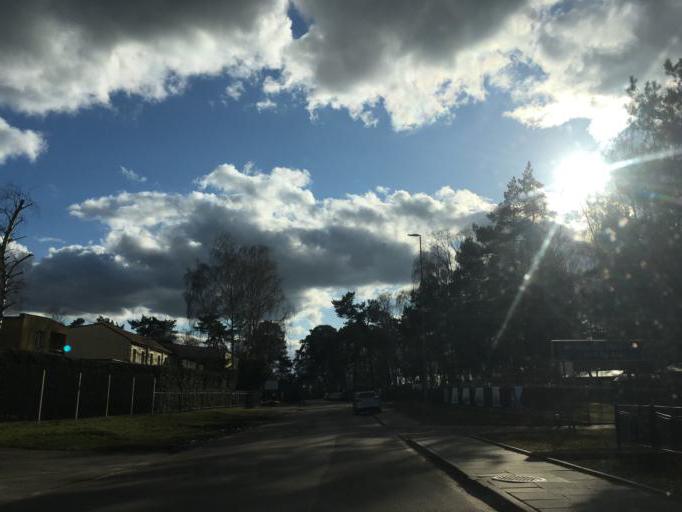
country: PL
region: Pomeranian Voivodeship
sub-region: Powiat gdanski
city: Cedry Wielkie
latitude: 54.3451
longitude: 18.8353
